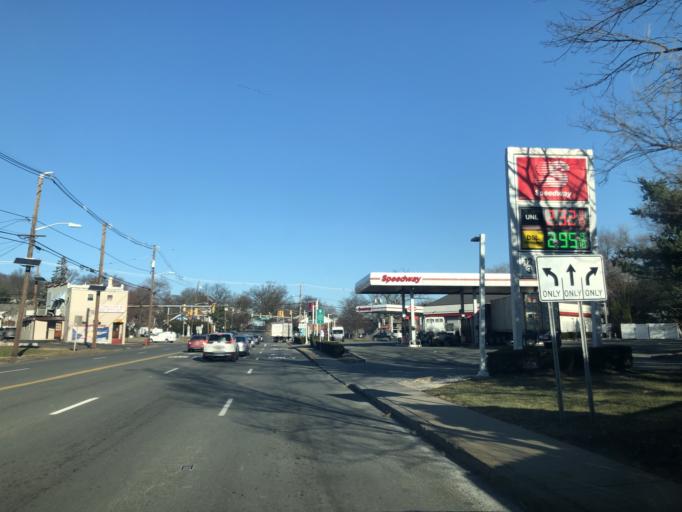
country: US
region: New Jersey
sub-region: Middlesex County
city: Fords
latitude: 40.5305
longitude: -74.3267
